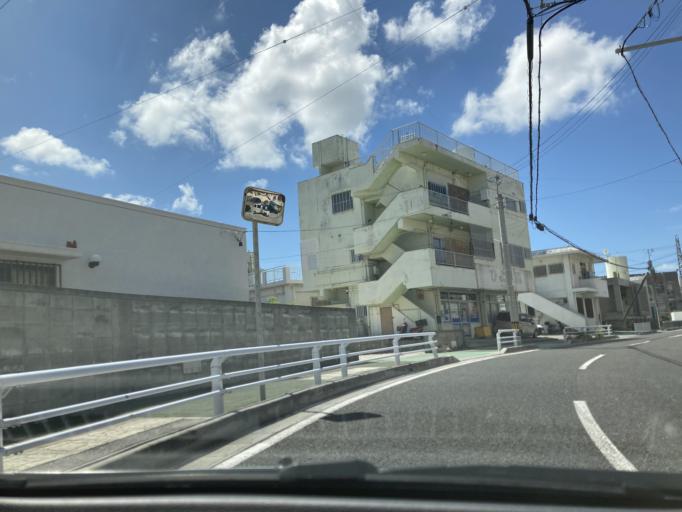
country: JP
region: Okinawa
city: Tomigusuku
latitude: 26.1966
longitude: 127.6720
